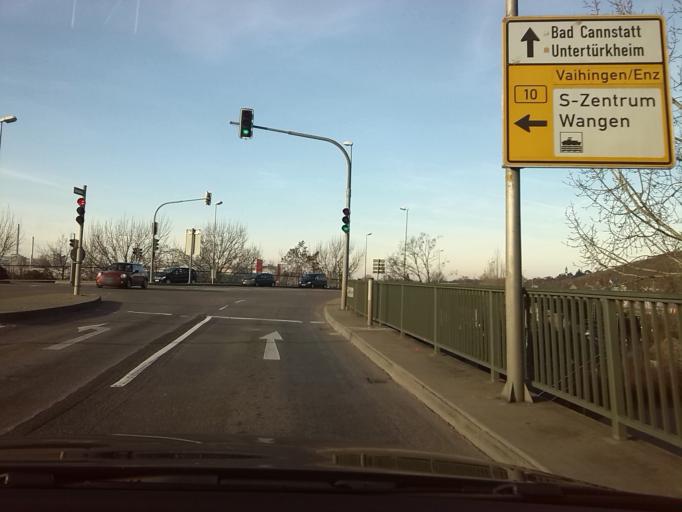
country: DE
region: Baden-Wuerttemberg
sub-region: Regierungsbezirk Stuttgart
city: Fellbach
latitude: 48.7718
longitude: 9.2590
